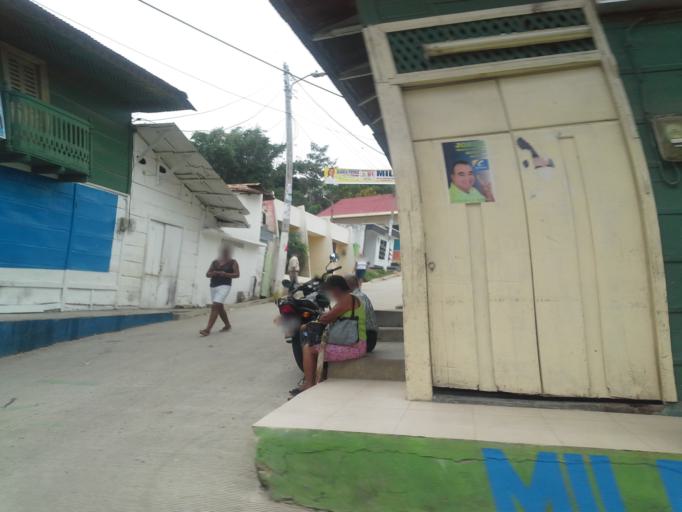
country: CO
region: Sucre
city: Ovejas
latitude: 9.5248
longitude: -75.2299
